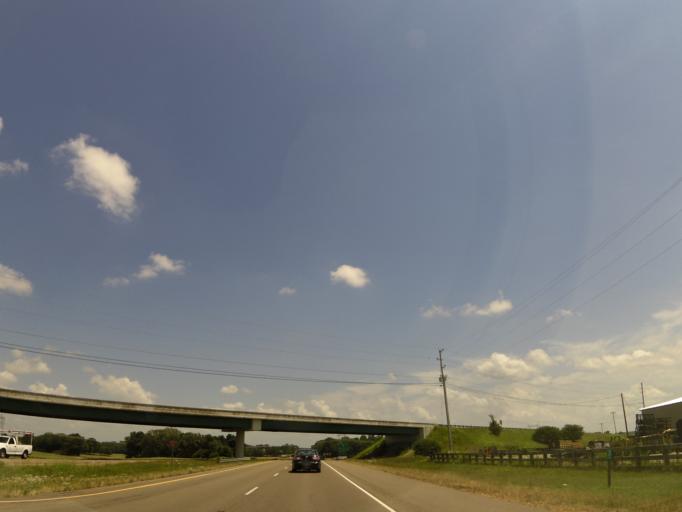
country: US
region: Tennessee
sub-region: Crockett County
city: Alamo
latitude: 35.8838
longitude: -89.2288
